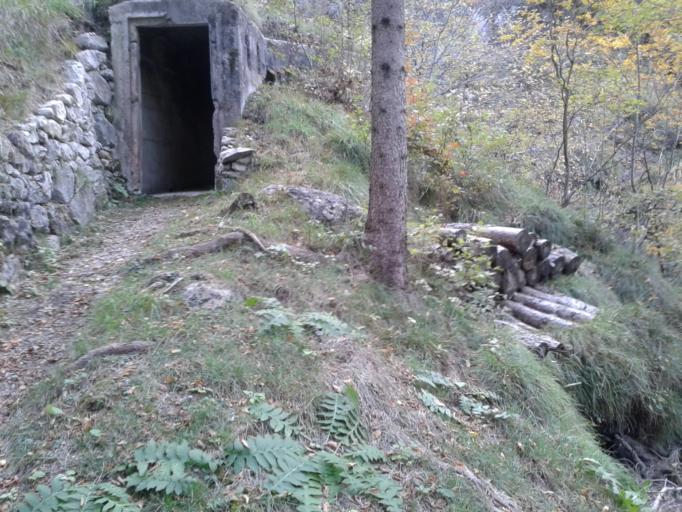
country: IT
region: Trentino-Alto Adige
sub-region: Provincia di Trento
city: Condino
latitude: 45.8767
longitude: 10.5998
